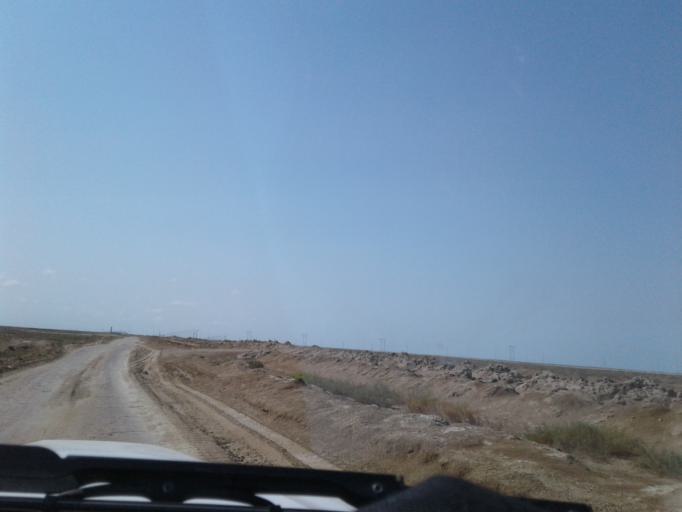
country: IR
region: Golestan
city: Gomishan
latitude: 37.8277
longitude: 53.9215
